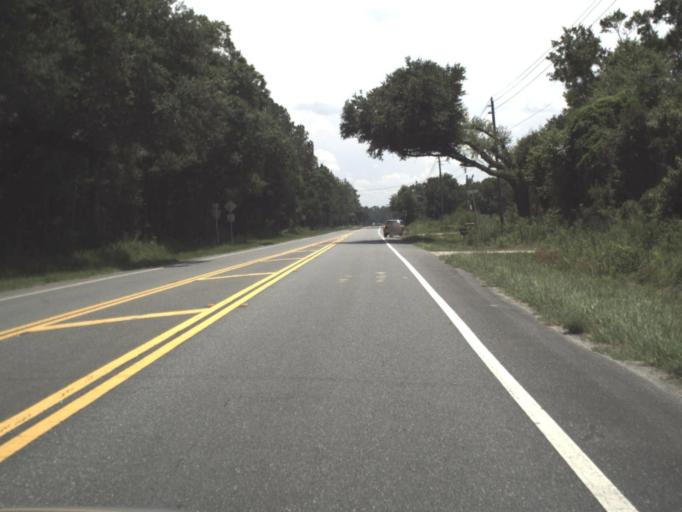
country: US
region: Florida
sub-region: Bradford County
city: Starke
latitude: 30.0383
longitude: -82.1646
